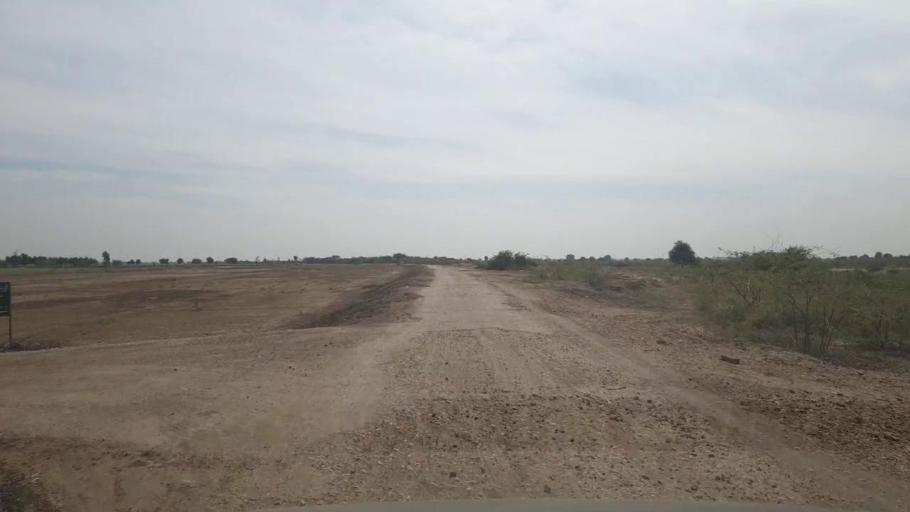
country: PK
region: Sindh
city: Kunri
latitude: 25.2782
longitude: 69.5972
